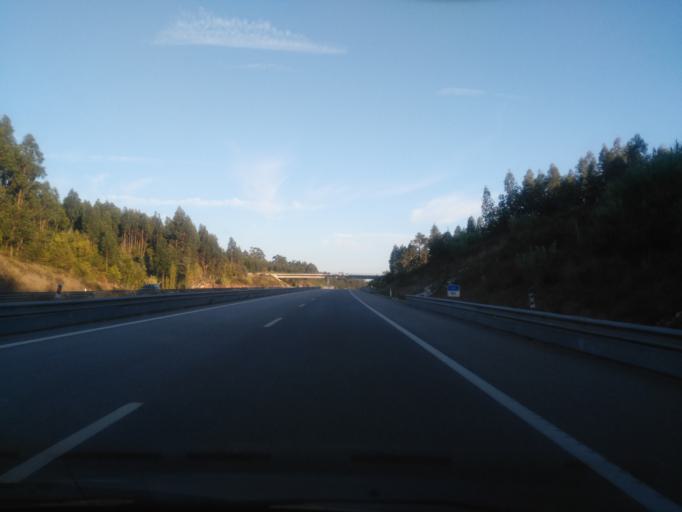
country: PT
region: Coimbra
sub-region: Figueira da Foz
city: Alhadas
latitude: 40.1727
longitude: -8.7931
